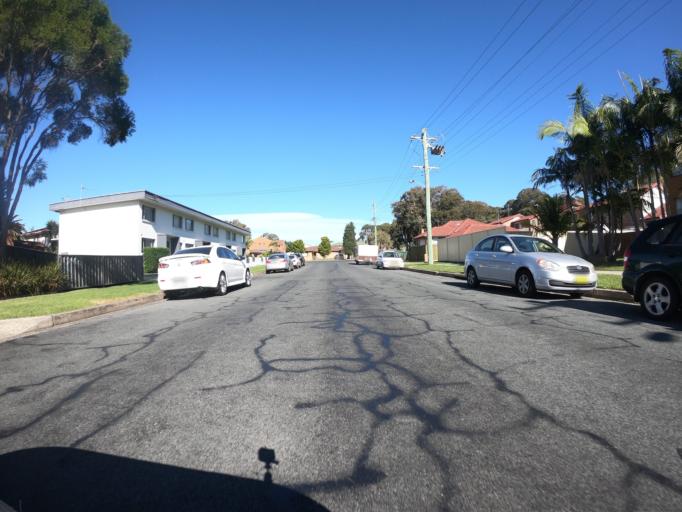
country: AU
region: New South Wales
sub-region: Wollongong
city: East Corrimal
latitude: -34.3737
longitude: 150.9074
